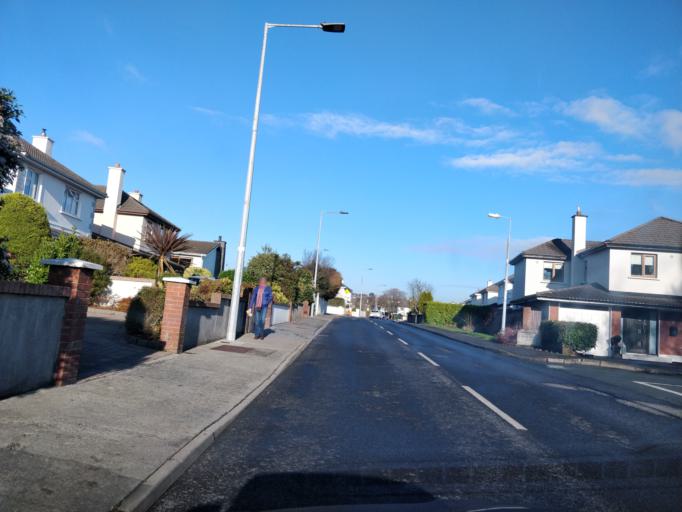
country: IE
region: Connaught
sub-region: County Galway
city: Bearna
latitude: 53.2616
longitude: -9.1173
